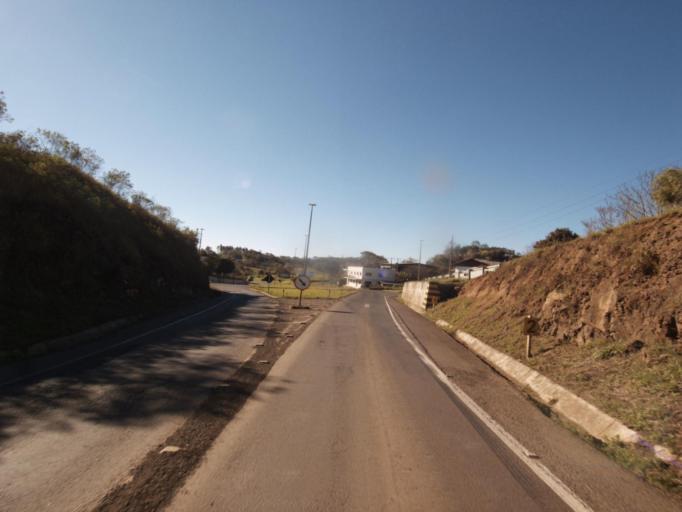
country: AR
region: Misiones
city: Bernardo de Irigoyen
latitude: -26.6569
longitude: -53.5173
